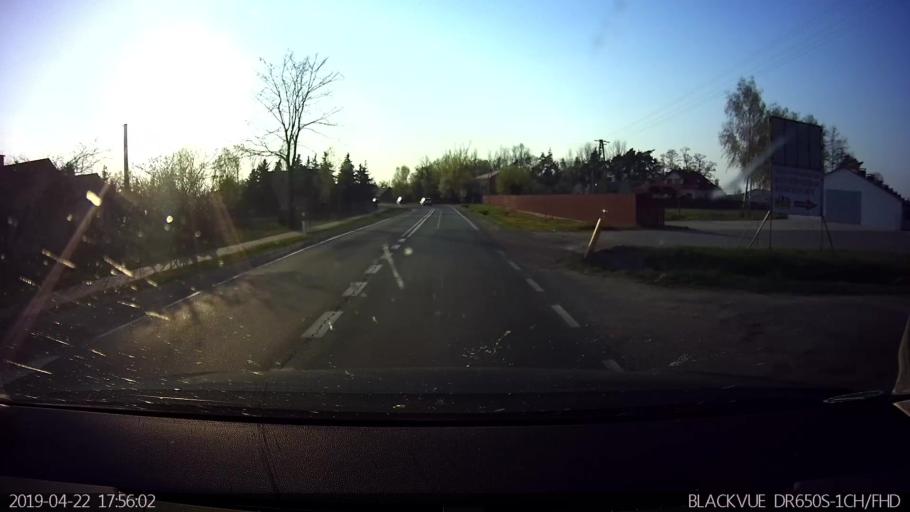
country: PL
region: Masovian Voivodeship
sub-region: Powiat wegrowski
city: Korytnica
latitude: 52.4639
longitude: 21.9126
